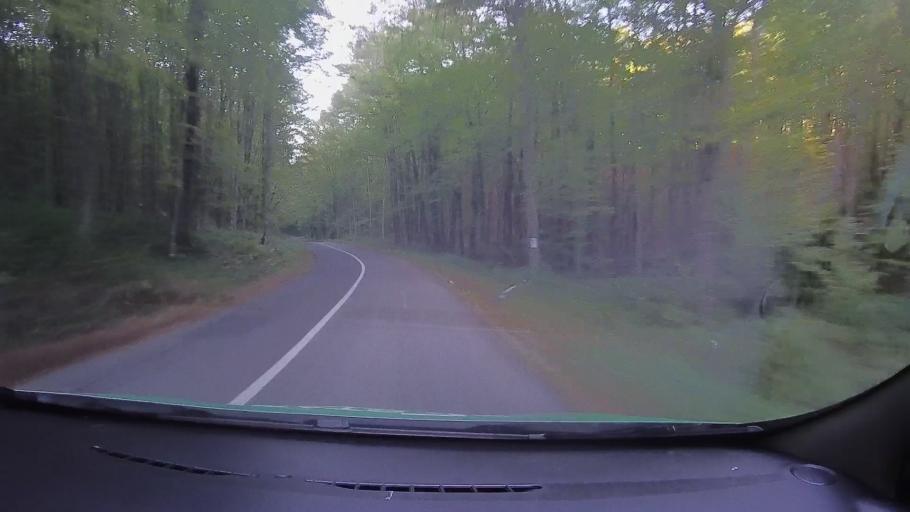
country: RO
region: Timis
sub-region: Comuna Nadrag
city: Nadrag
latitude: 45.6813
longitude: 22.1571
